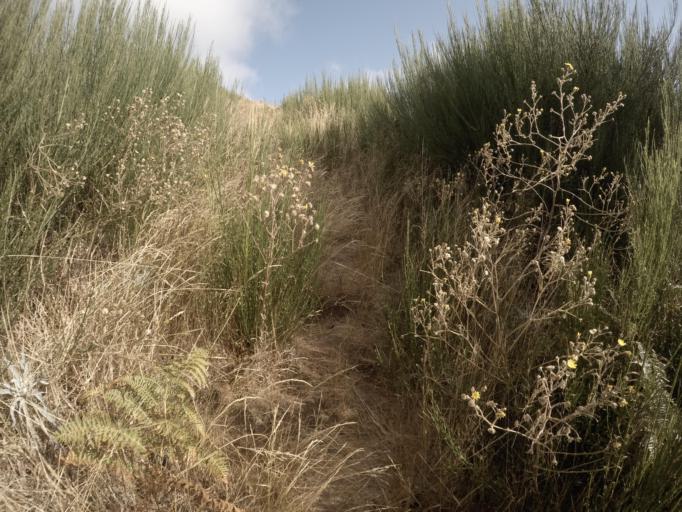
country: PT
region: Madeira
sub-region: Camara de Lobos
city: Curral das Freiras
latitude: 32.7123
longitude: -16.9893
